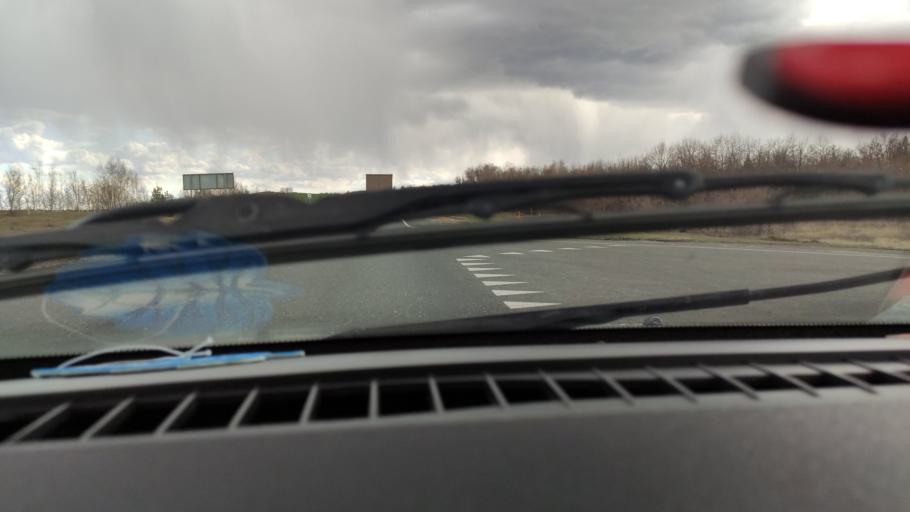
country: RU
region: Saratov
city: Balakovo
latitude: 52.1739
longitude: 47.8339
